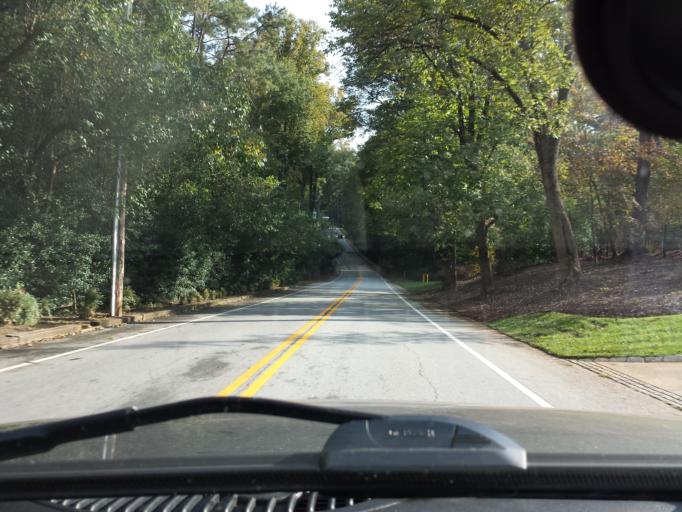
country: US
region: Georgia
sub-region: Cobb County
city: Vinings
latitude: 33.8871
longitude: -84.4266
